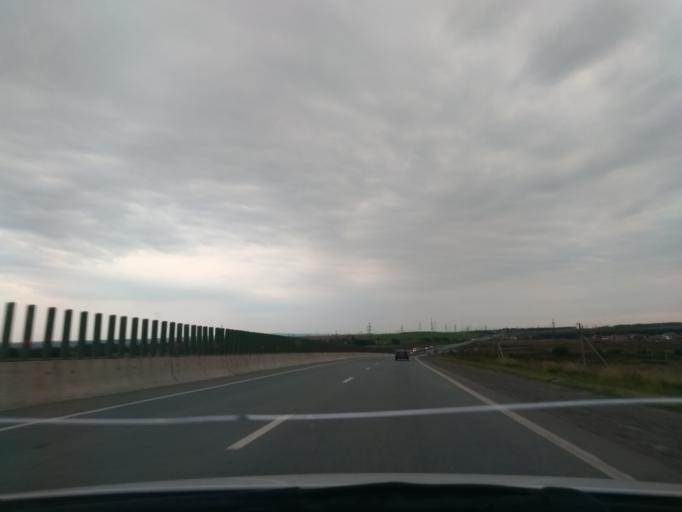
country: RU
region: Perm
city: Ferma
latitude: 57.9338
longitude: 56.3520
